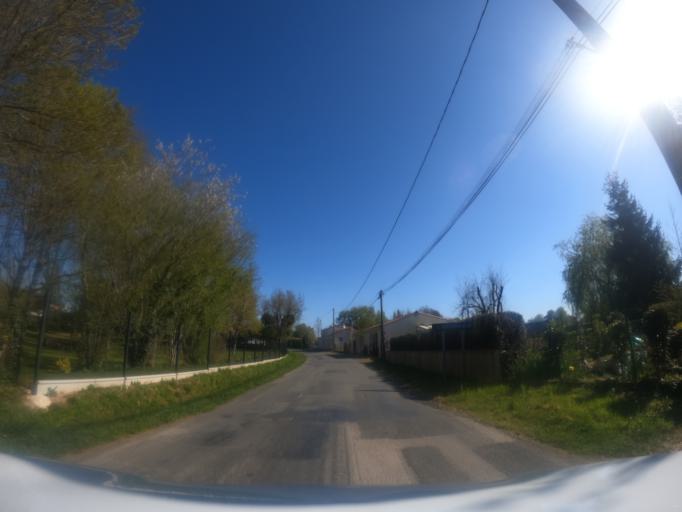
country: FR
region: Pays de la Loire
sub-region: Departement de la Vendee
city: Le Champ-Saint-Pere
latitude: 46.5347
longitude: -1.3502
